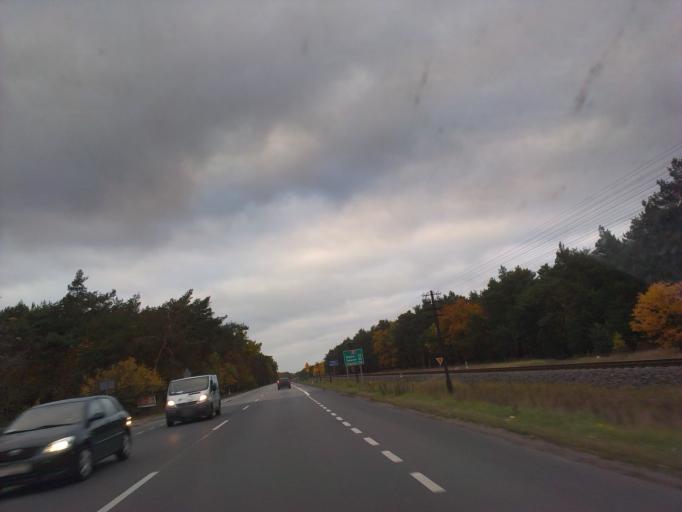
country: PL
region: Kujawsko-Pomorskie
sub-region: Powiat torunski
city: Lysomice
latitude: 53.0570
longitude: 18.6177
